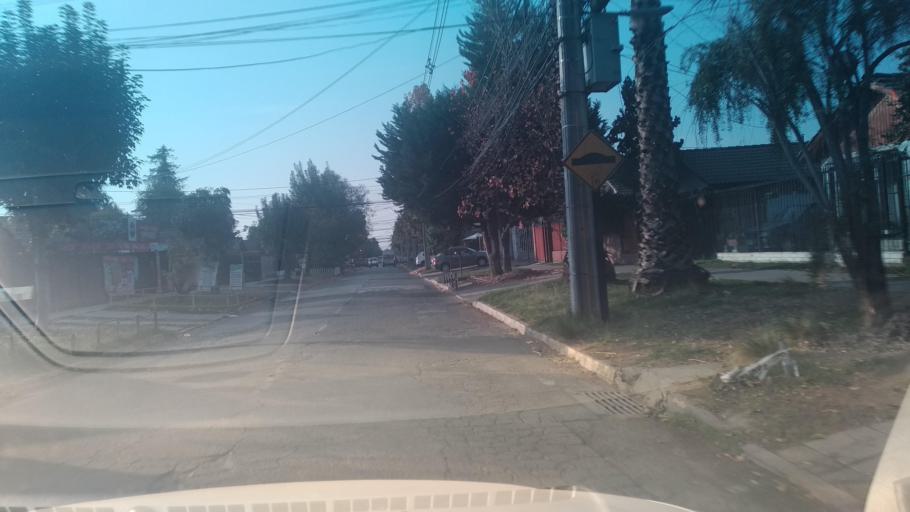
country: CL
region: Santiago Metropolitan
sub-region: Provincia de Santiago
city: Lo Prado
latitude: -33.3625
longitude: -70.7140
